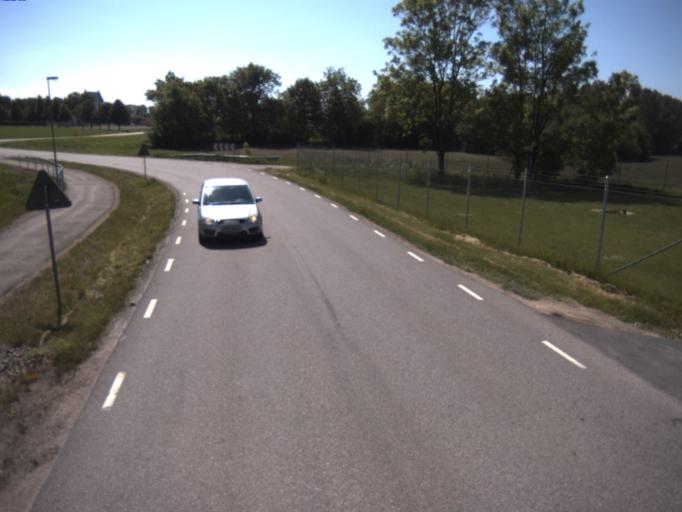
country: SE
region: Skane
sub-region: Helsingborg
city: Barslov
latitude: 56.0223
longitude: 12.8005
